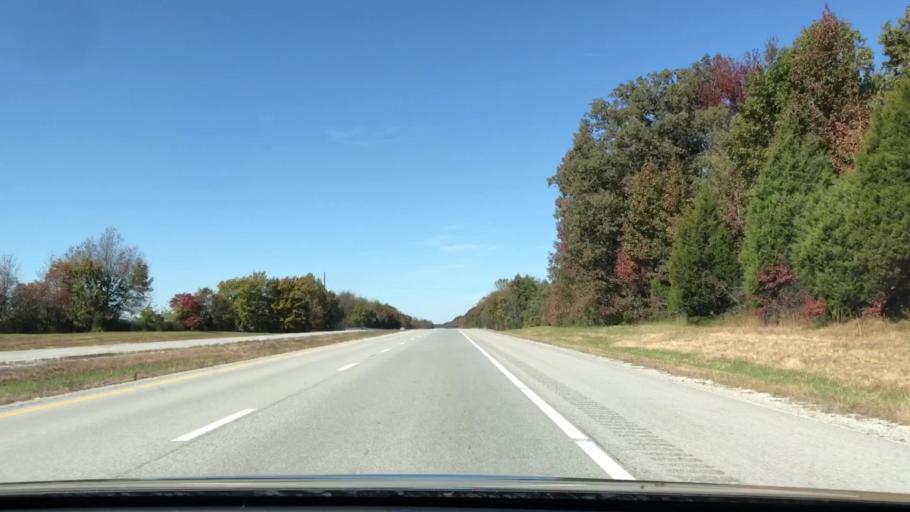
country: US
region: Kentucky
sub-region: Barren County
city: Glasgow
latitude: 37.0278
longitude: -86.0462
